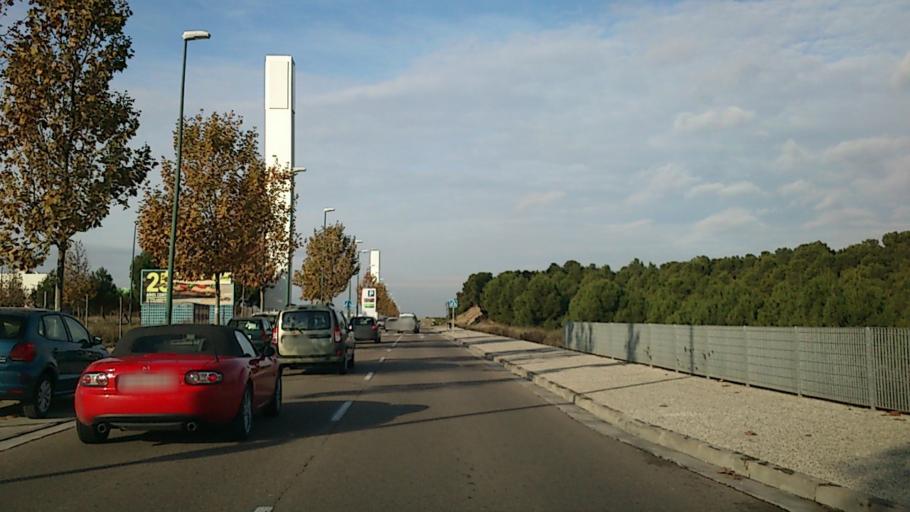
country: ES
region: Aragon
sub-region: Provincia de Zaragoza
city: Delicias
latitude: 41.6106
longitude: -0.8851
